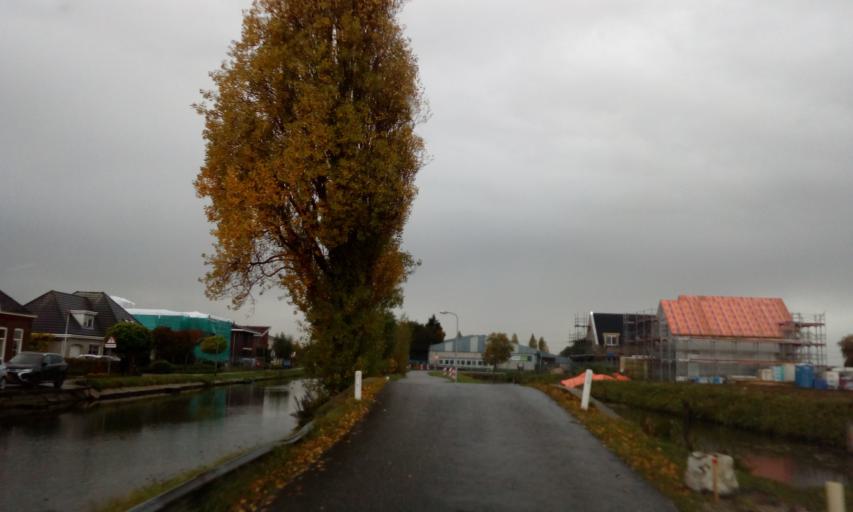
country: NL
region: South Holland
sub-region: Gemeente Rijswijk
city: Rijswijk
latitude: 52.0138
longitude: 4.3279
